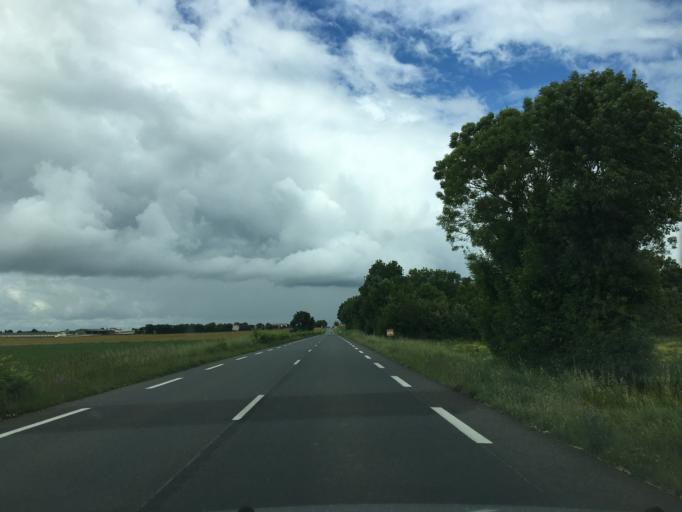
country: FR
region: Poitou-Charentes
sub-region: Departement de la Charente-Maritime
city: Saint-Jean-d'Angely
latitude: 46.0653
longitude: -0.5080
